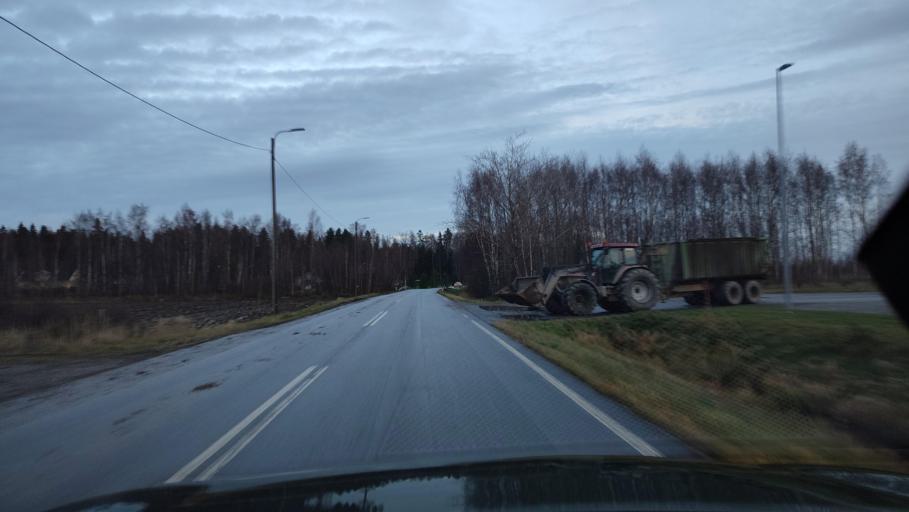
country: FI
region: Ostrobothnia
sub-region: Vaasa
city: Ristinummi
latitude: 63.0484
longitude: 21.7325
